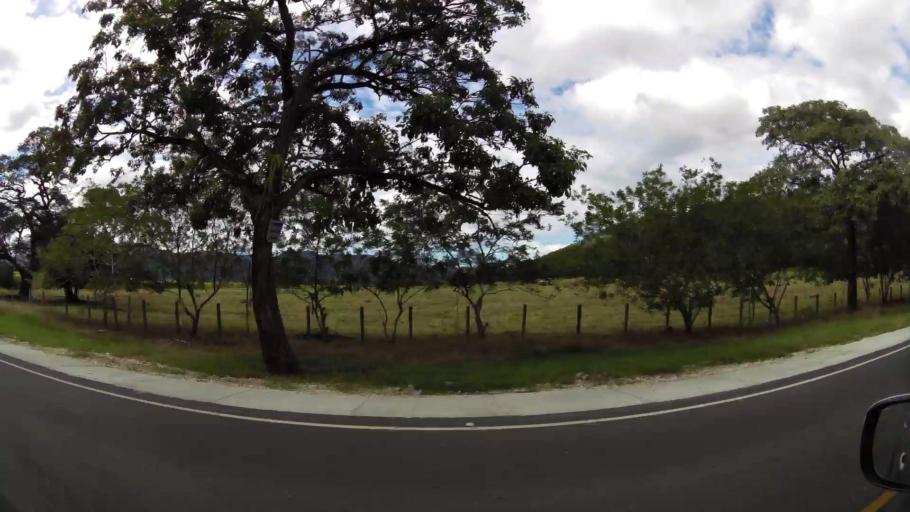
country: CR
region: Guanacaste
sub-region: Canton de Nicoya
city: Nicoya
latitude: 10.1547
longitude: -85.3100
